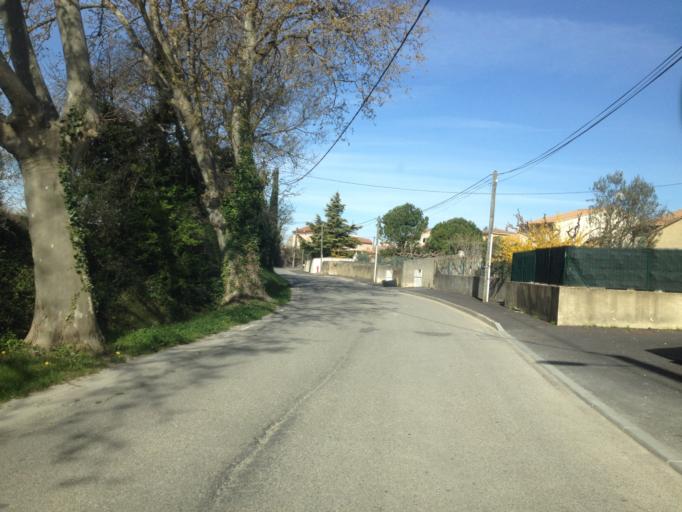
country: FR
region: Provence-Alpes-Cote d'Azur
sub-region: Departement du Vaucluse
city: Caderousse
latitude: 44.1013
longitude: 4.7605
